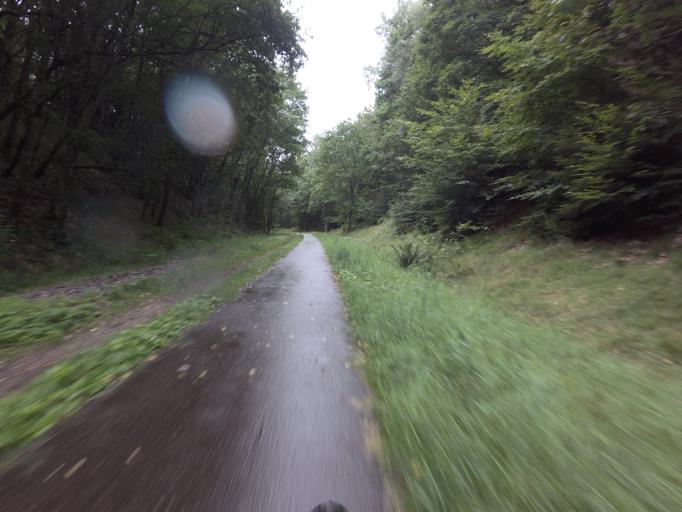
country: DK
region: Central Jutland
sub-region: Silkeborg Kommune
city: Silkeborg
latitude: 56.1301
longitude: 9.4239
